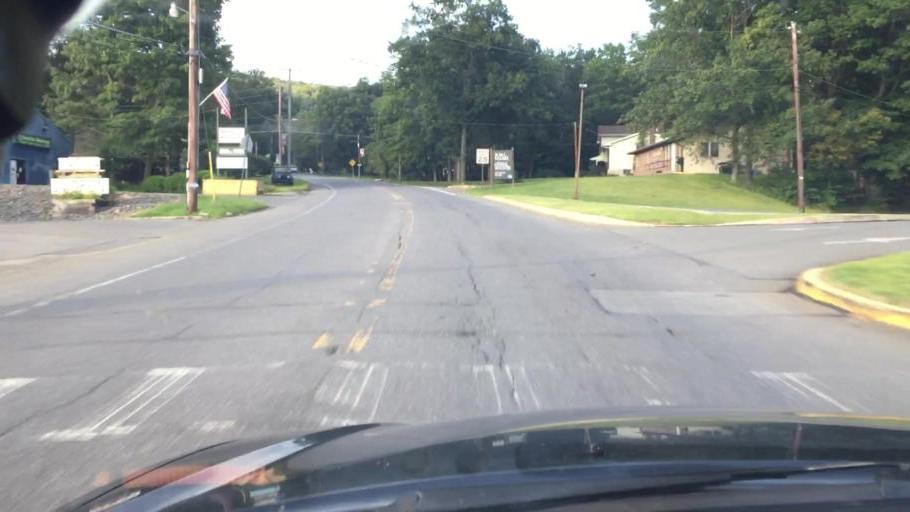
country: US
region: Pennsylvania
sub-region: Carbon County
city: Jim Thorpe
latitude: 40.8818
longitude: -75.7262
